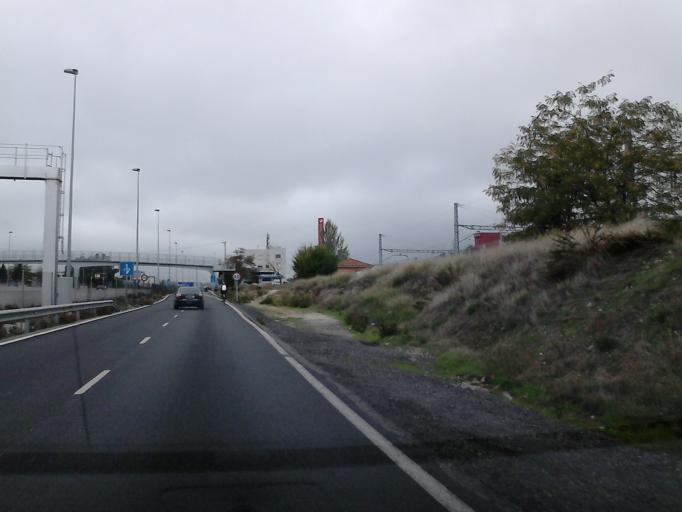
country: ES
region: Madrid
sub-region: Provincia de Madrid
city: Las Matas
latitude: 40.5507
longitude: -3.8967
